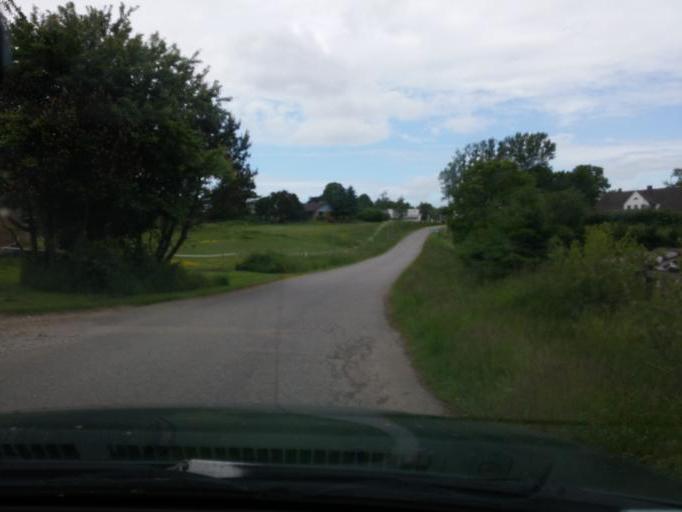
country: DK
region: South Denmark
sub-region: Aabenraa Kommune
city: Lojt Kirkeby
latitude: 55.1377
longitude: 9.4901
